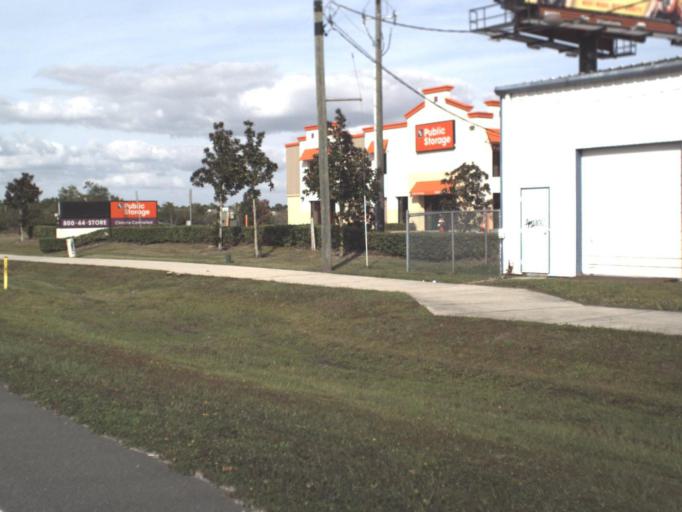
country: US
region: Florida
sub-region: Osceola County
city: Kissimmee
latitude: 28.3289
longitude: -81.4160
